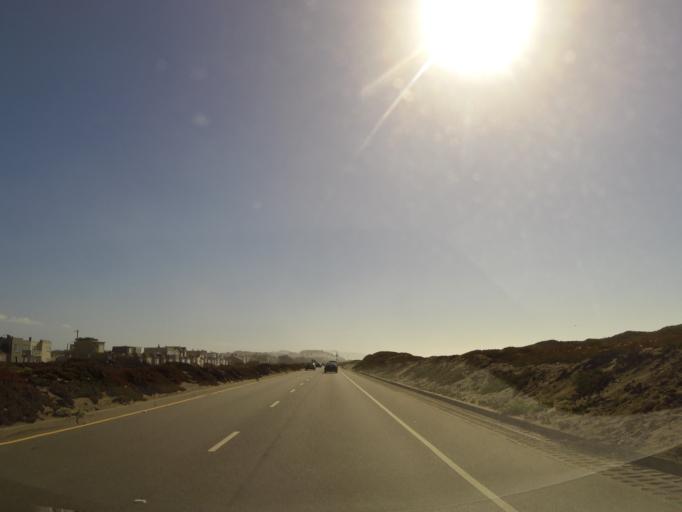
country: US
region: California
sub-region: San Mateo County
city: Daly City
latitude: 37.7411
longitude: -122.5075
